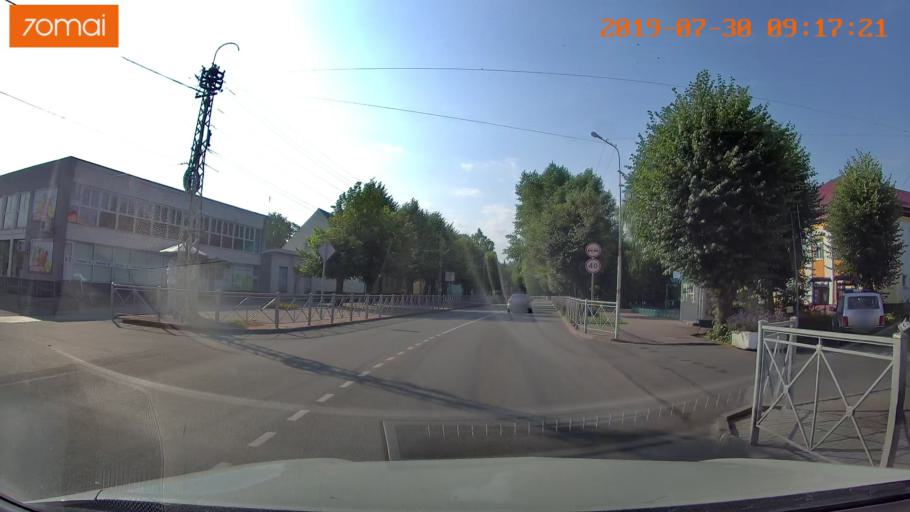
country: RU
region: Kaliningrad
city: Nesterov
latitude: 54.6342
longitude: 22.5680
